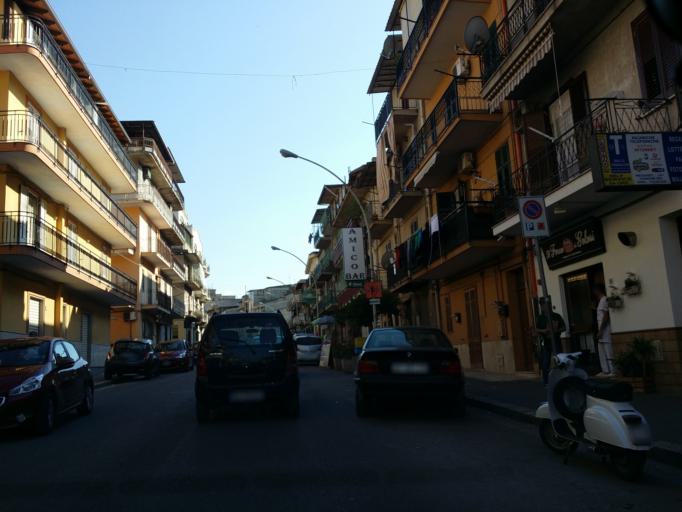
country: IT
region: Sicily
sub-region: Palermo
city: Misilmeri
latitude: 38.0286
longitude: 13.4491
